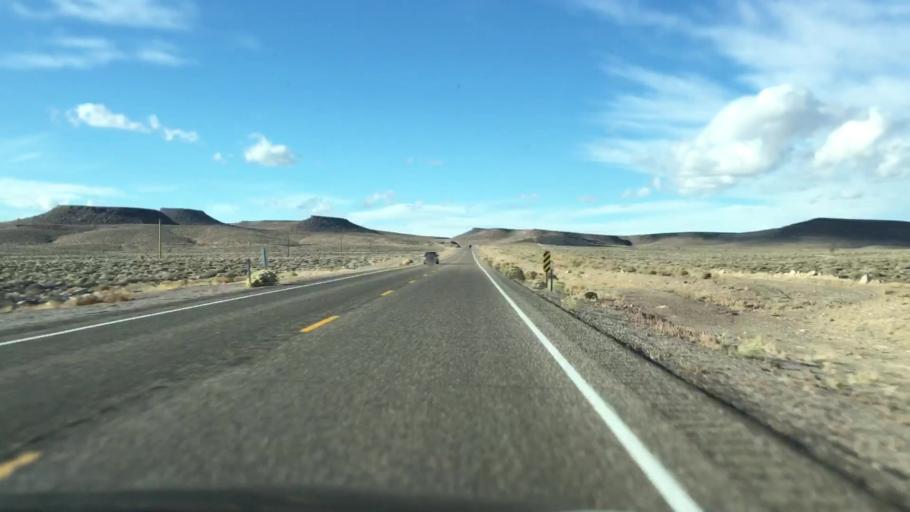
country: US
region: Nevada
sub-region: Esmeralda County
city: Goldfield
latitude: 37.3704
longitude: -117.1259
